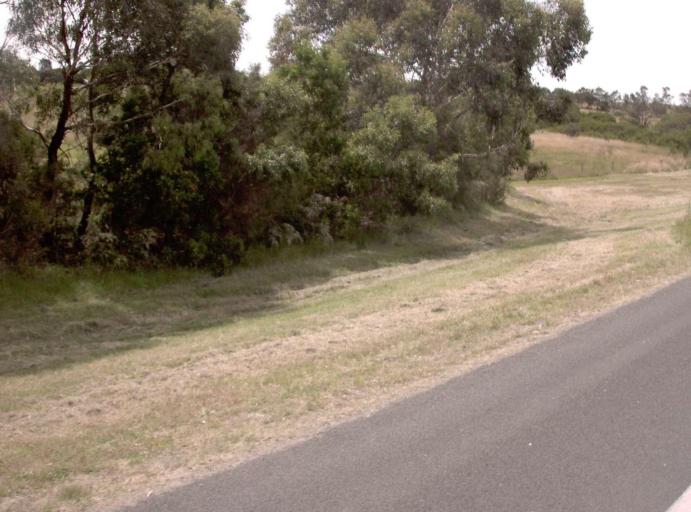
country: AU
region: Victoria
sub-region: Mornington Peninsula
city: Mount Martha
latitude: -38.2824
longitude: 145.0535
